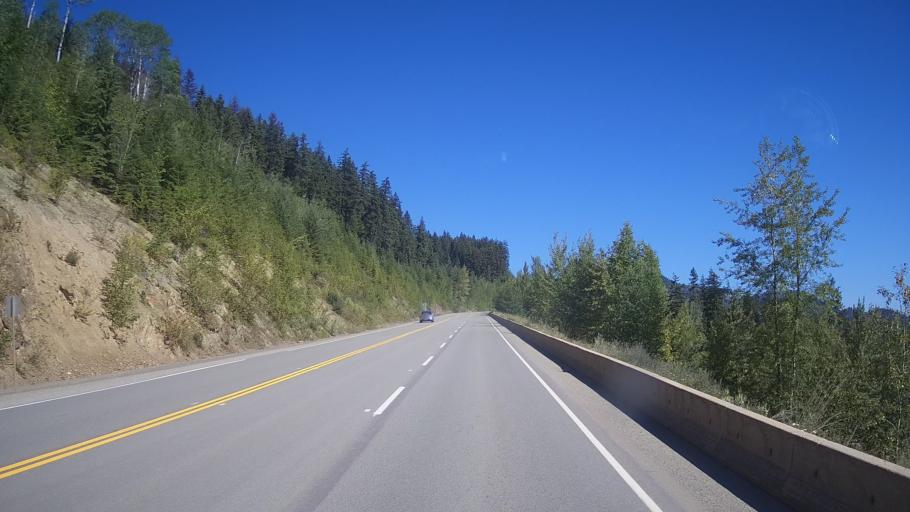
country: CA
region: British Columbia
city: Kamloops
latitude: 51.4719
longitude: -120.2559
